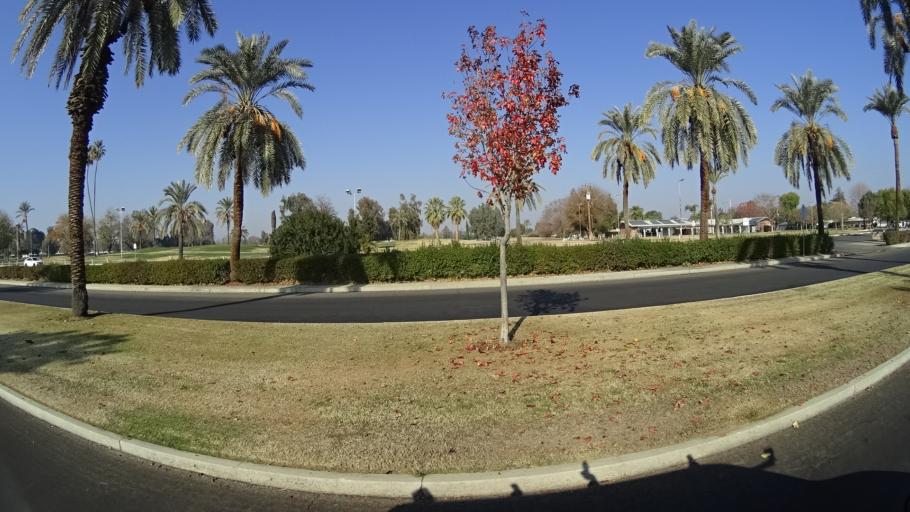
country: US
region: California
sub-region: Kern County
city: Greenacres
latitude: 35.3439
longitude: -119.0681
